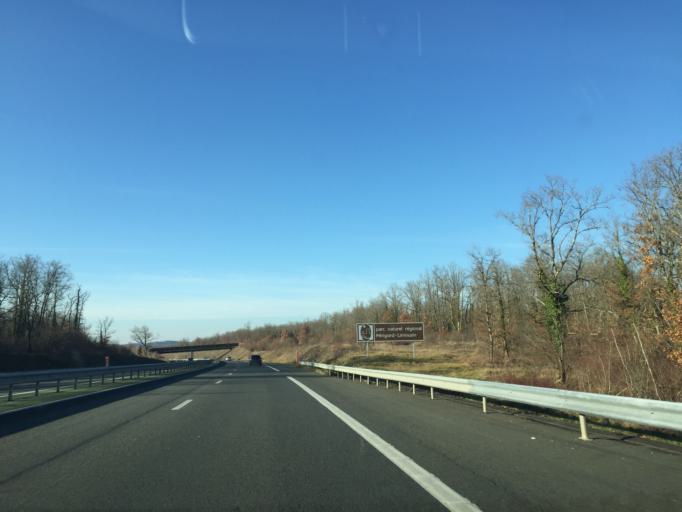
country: FR
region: Aquitaine
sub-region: Departement de la Dordogne
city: Thenon
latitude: 45.1723
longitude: 1.0246
